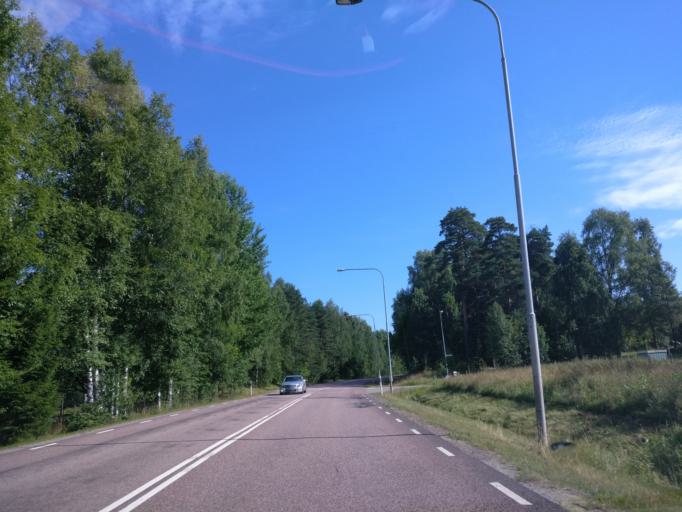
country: SE
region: Vaermland
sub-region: Hagfors Kommun
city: Hagfors
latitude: 60.0549
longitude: 13.7052
